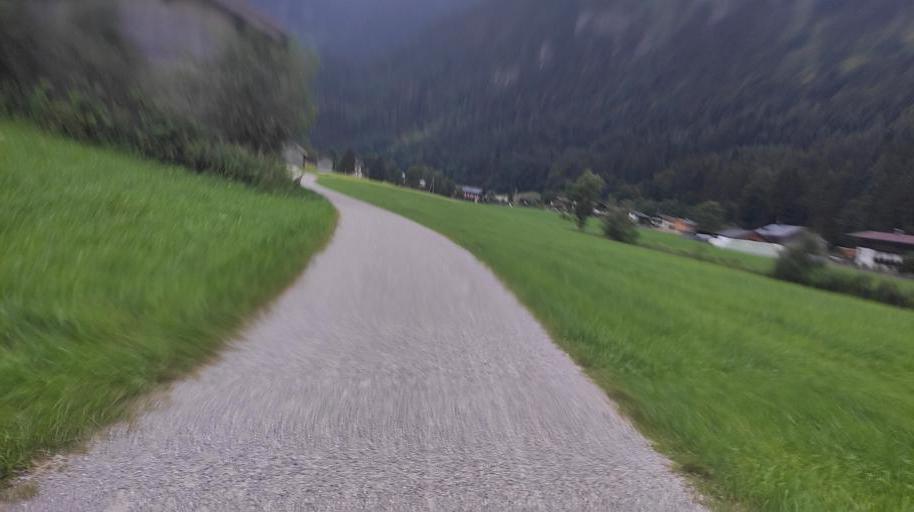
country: AT
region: Salzburg
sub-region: Politischer Bezirk Zell am See
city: Lofer
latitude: 47.5780
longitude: 12.6908
